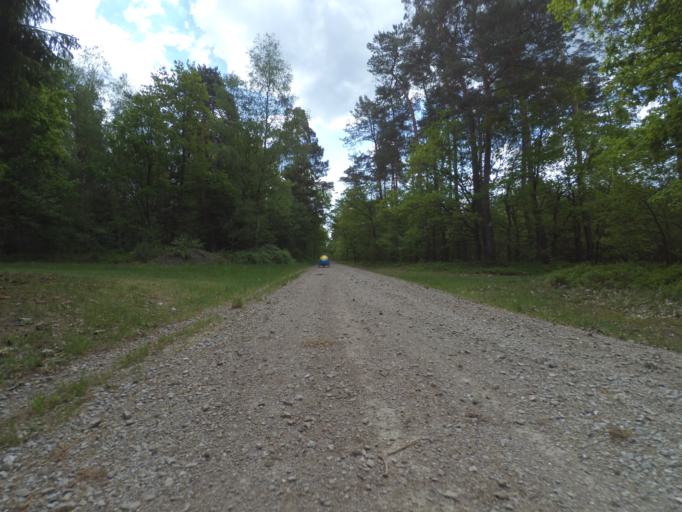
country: DE
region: Lower Saxony
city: Isernhagen Farster Bauerschaft
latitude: 52.5615
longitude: 9.8822
